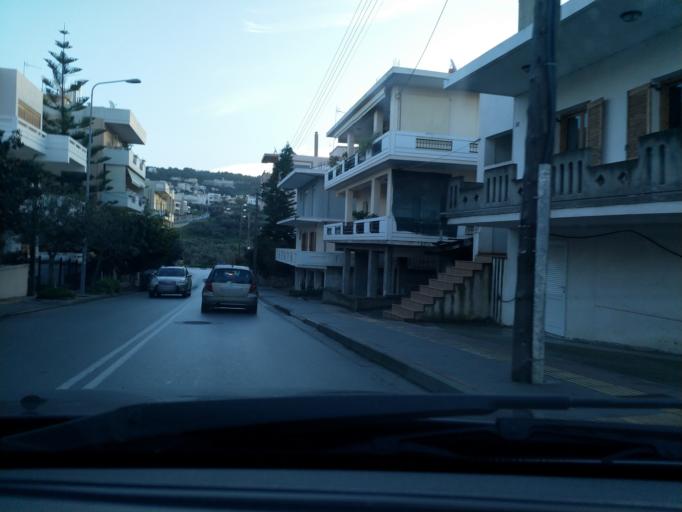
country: GR
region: Crete
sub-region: Nomos Chanias
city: Chania
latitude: 35.5118
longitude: 24.0435
